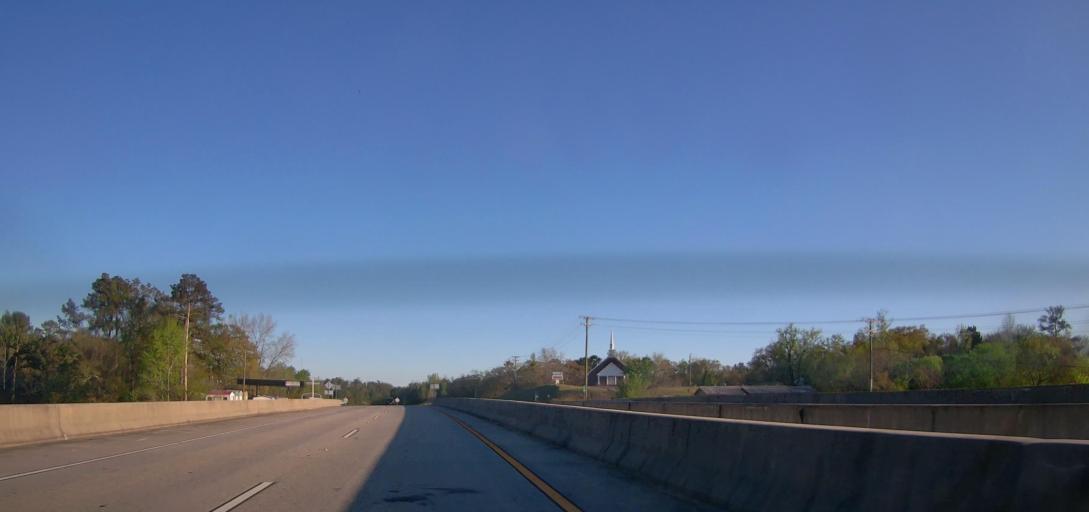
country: US
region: Georgia
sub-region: Wilkinson County
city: Irwinton
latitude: 32.8465
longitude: -83.1923
